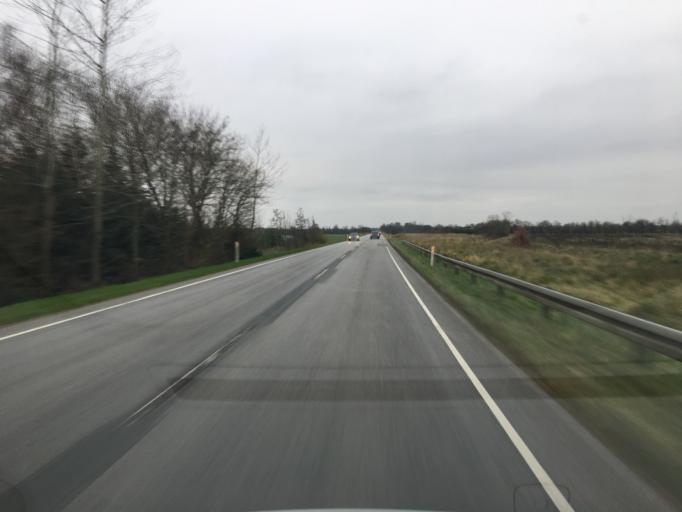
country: DK
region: South Denmark
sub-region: Aabenraa Kommune
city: Tinglev
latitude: 54.9867
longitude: 9.1765
